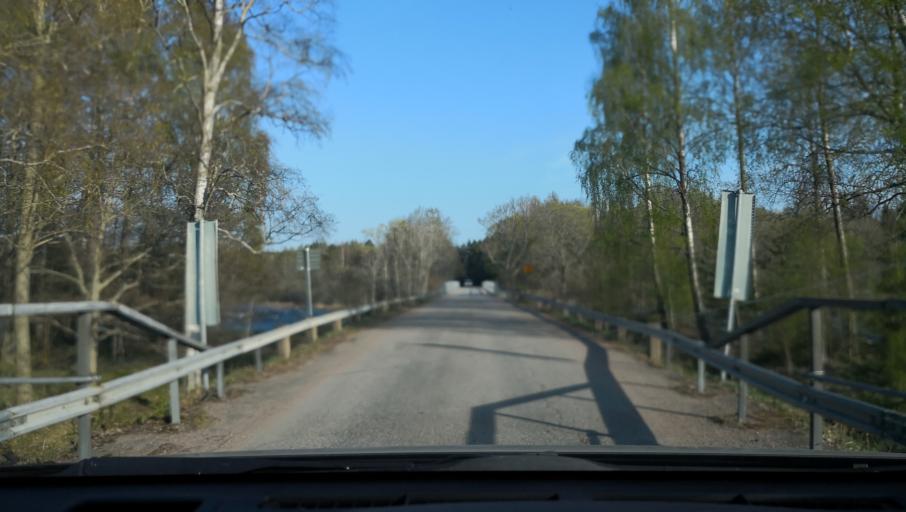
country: SE
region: Uppsala
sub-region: Heby Kommun
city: Tarnsjo
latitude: 60.2680
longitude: 16.9130
